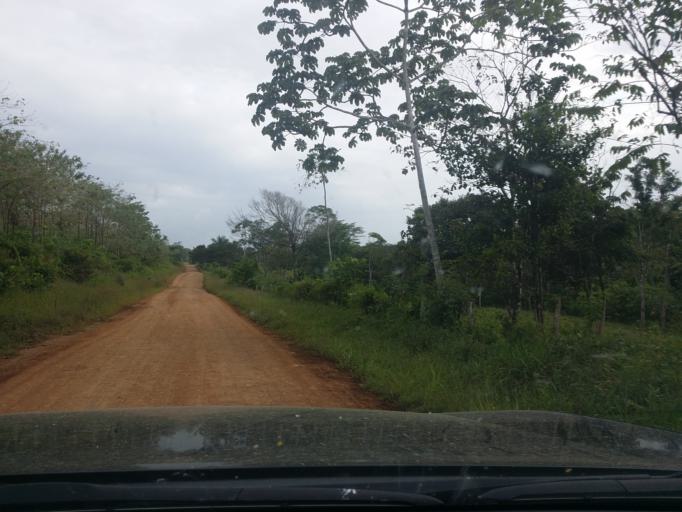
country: CR
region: Alajuela
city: Los Chiles
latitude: 11.0566
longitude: -84.4845
